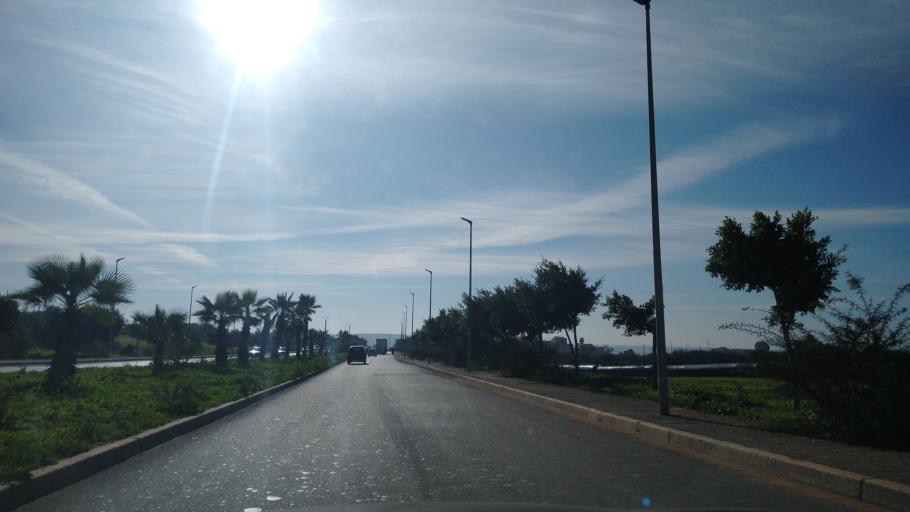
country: MA
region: Rabat-Sale-Zemmour-Zaer
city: Sale
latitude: 34.0018
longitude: -6.7490
